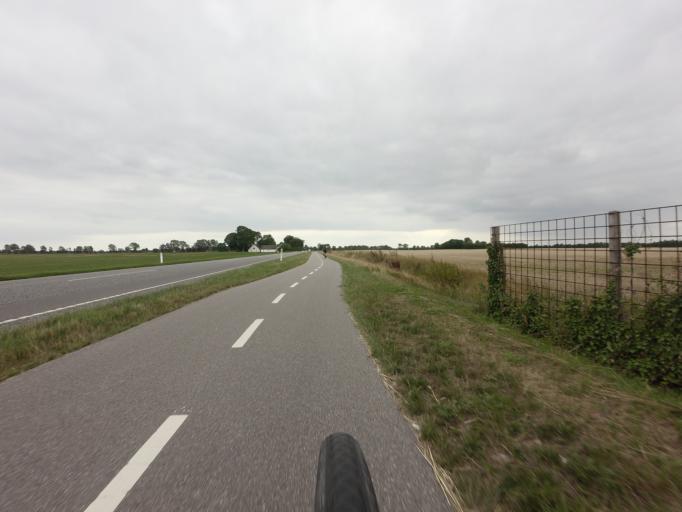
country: DK
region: Zealand
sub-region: Stevns Kommune
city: Store Heddinge
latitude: 55.2861
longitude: 12.3912
